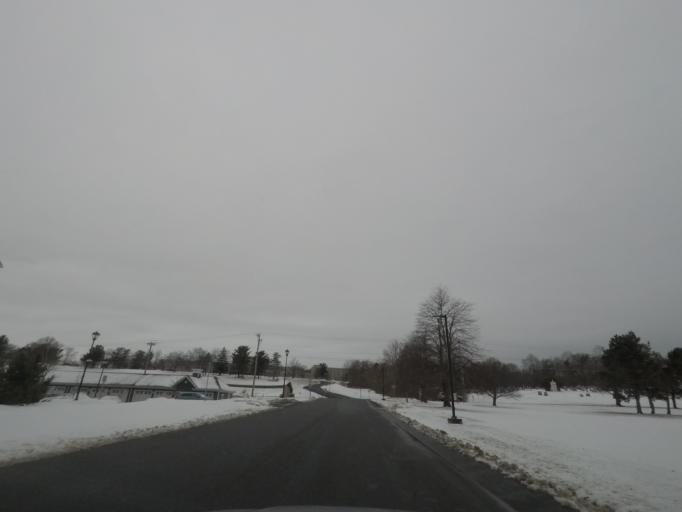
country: US
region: New York
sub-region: Albany County
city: Watervliet
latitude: 42.7330
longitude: -73.7335
